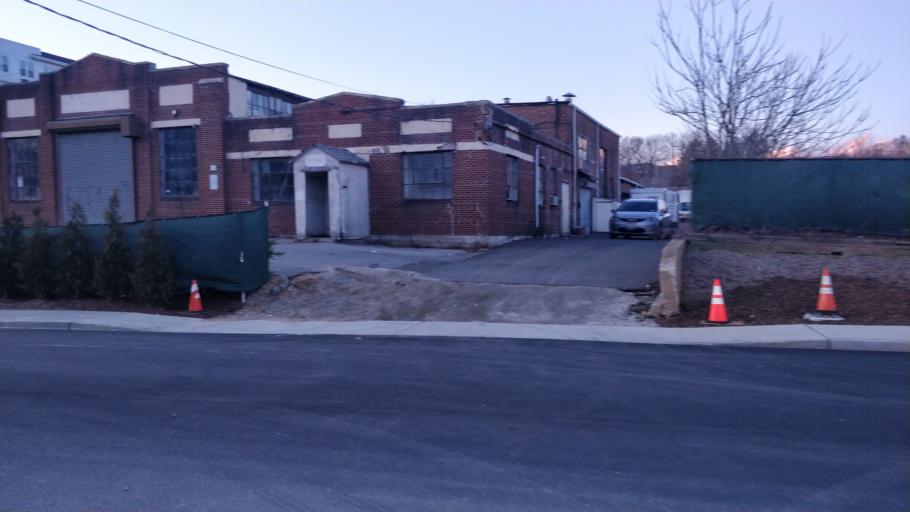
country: US
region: New York
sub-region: Nassau County
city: Glen Cove
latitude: 40.8617
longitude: -73.6385
